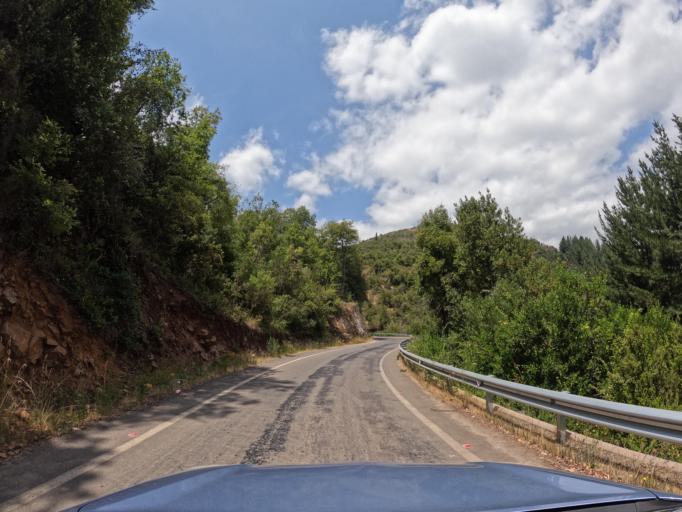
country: CL
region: Maule
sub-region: Provincia de Curico
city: Molina
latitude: -35.1766
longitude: -71.0861
